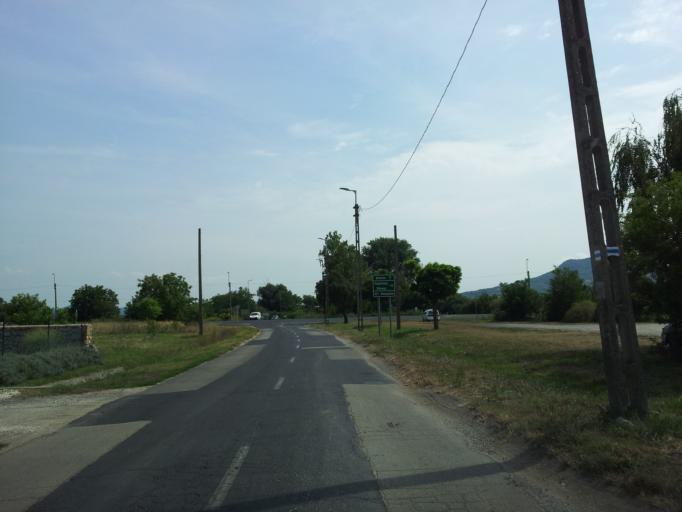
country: HU
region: Veszprem
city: Tapolca
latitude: 46.8778
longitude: 17.4443
